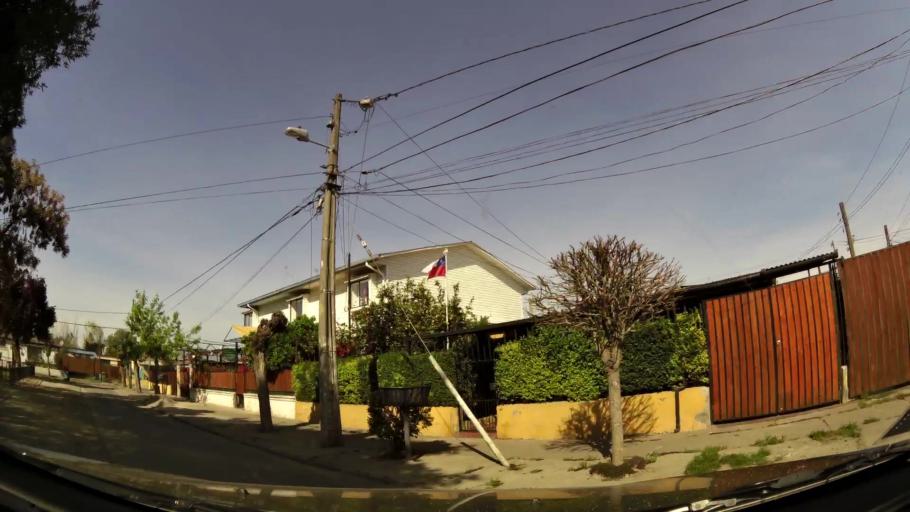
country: CL
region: Santiago Metropolitan
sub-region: Provincia de Cordillera
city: Puente Alto
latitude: -33.6059
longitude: -70.5898
